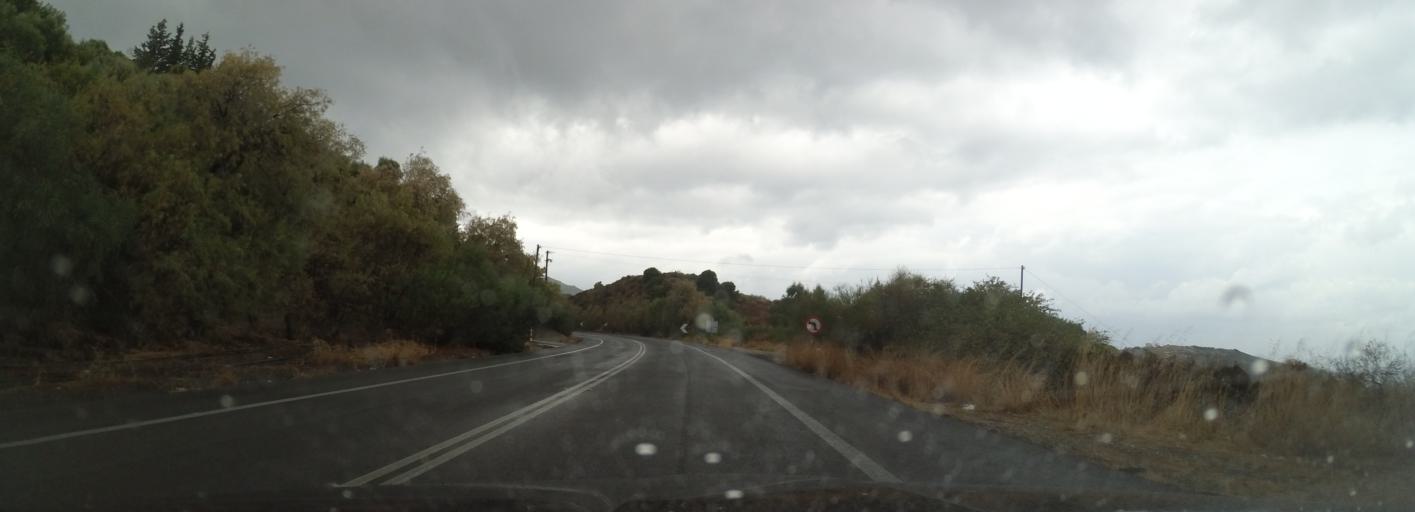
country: GR
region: Crete
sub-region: Nomos Irakleiou
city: Gazi
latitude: 35.4006
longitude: 25.0065
